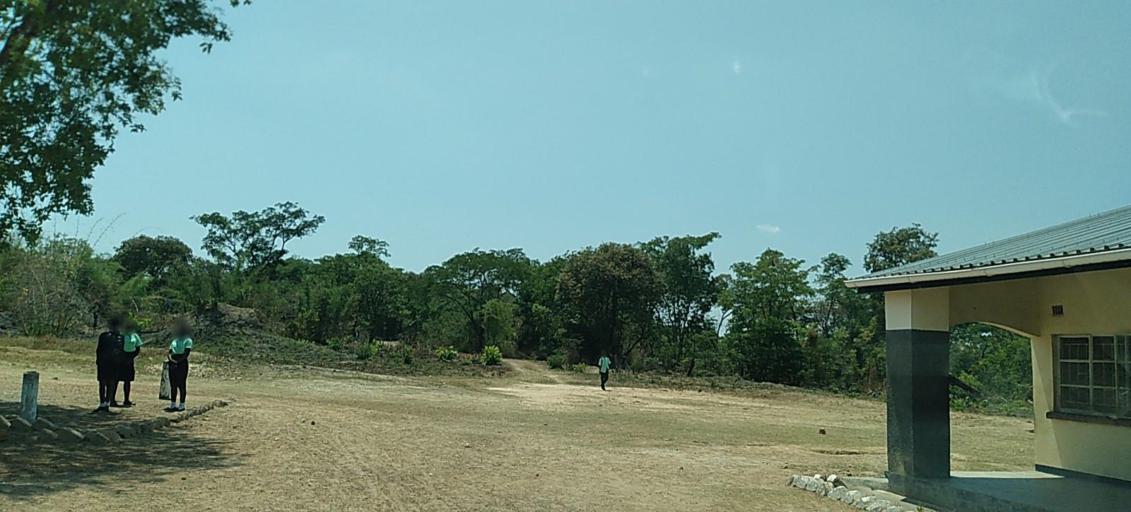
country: ZM
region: Copperbelt
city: Luanshya
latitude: -12.9937
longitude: 28.3268
